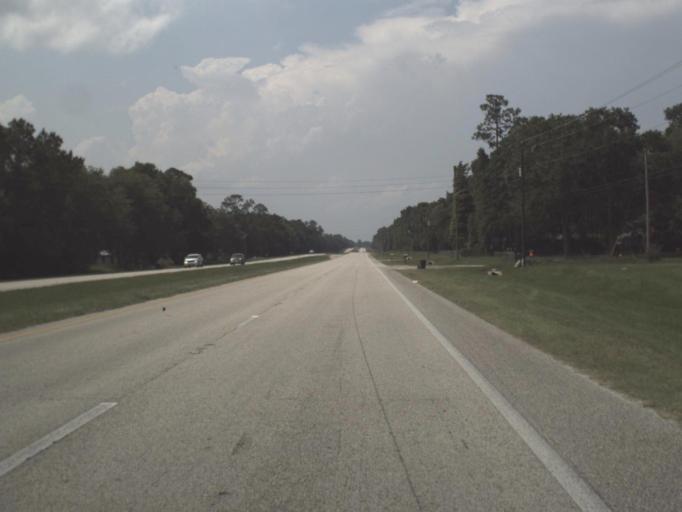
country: US
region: Florida
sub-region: Clay County
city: Green Cove Springs
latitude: 29.9119
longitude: -81.6786
